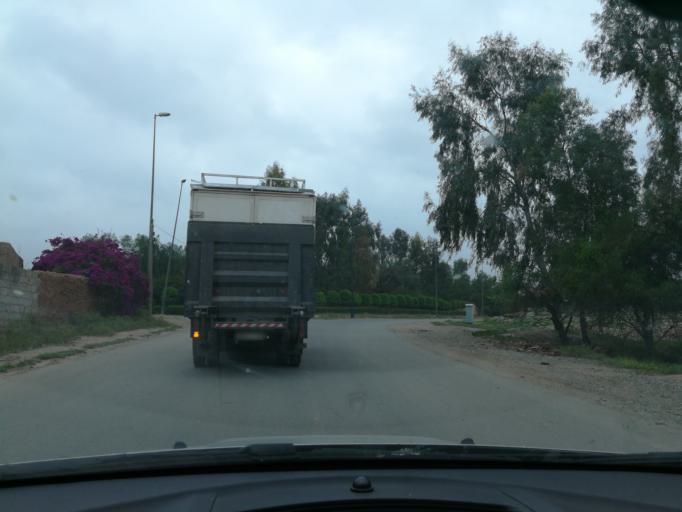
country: MA
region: Marrakech-Tensift-Al Haouz
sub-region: Marrakech
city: Marrakesh
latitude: 31.6570
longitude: -7.9833
